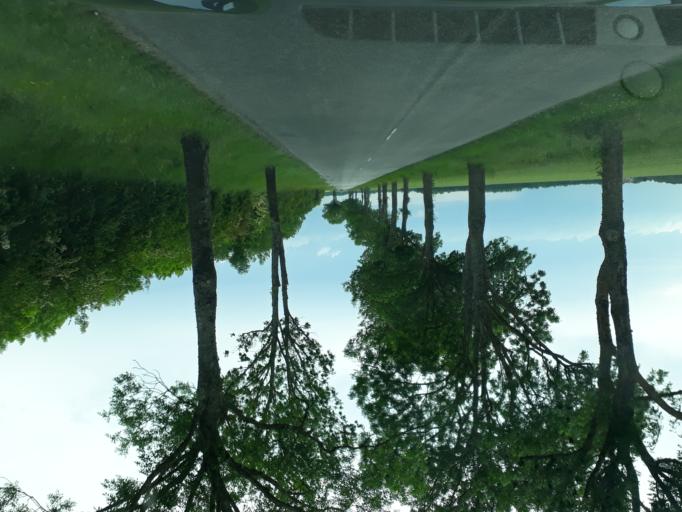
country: FR
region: Centre
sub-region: Departement du Loiret
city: Tigy
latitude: 47.8053
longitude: 2.1863
